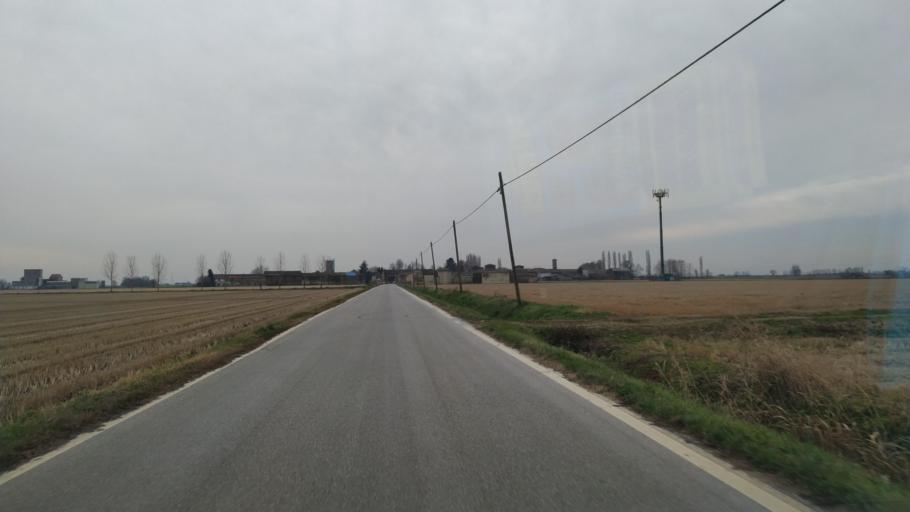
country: IT
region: Piedmont
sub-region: Provincia di Vercelli
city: Sali Vercellese
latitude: 45.3151
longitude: 8.3313
